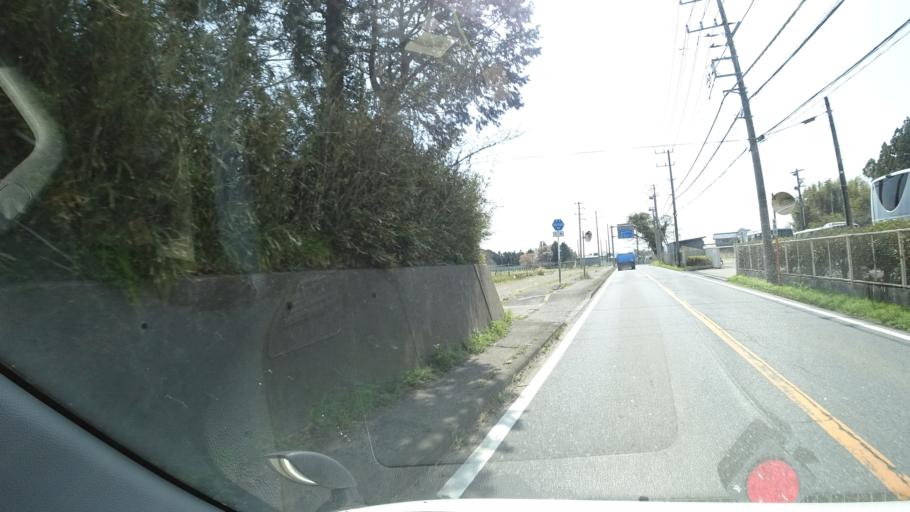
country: JP
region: Chiba
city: Narita
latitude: 35.7725
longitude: 140.3528
